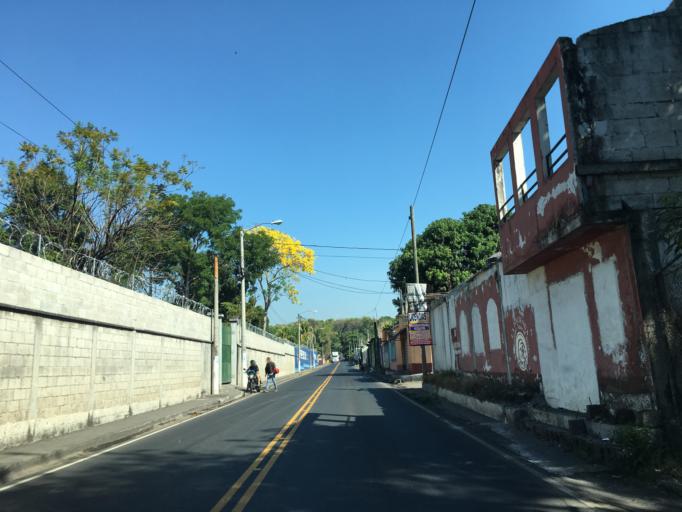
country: GT
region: Escuintla
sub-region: Municipio de La Democracia
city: La Democracia
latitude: 14.2310
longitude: -90.9496
